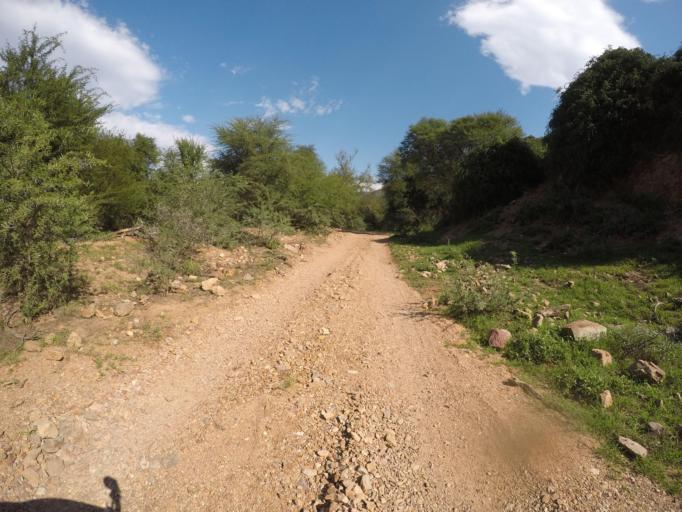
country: ZA
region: Eastern Cape
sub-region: Cacadu District Municipality
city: Kareedouw
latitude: -33.6632
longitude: 24.3907
